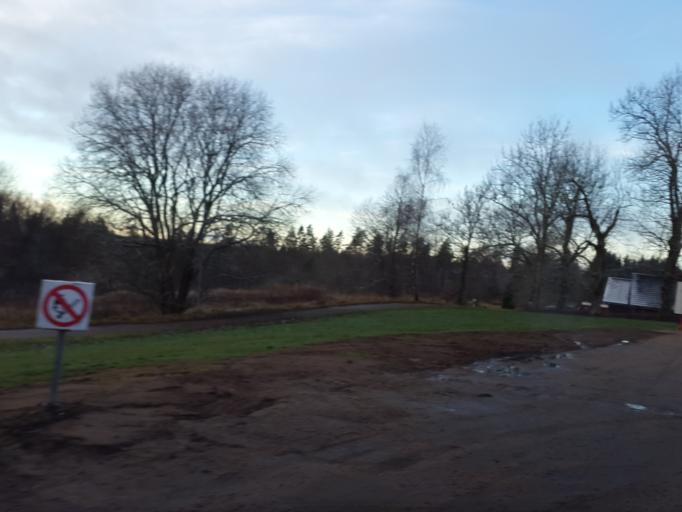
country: SE
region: Vaestra Goetaland
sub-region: Boras Kommun
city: Sjomarken
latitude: 57.7694
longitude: 12.8206
